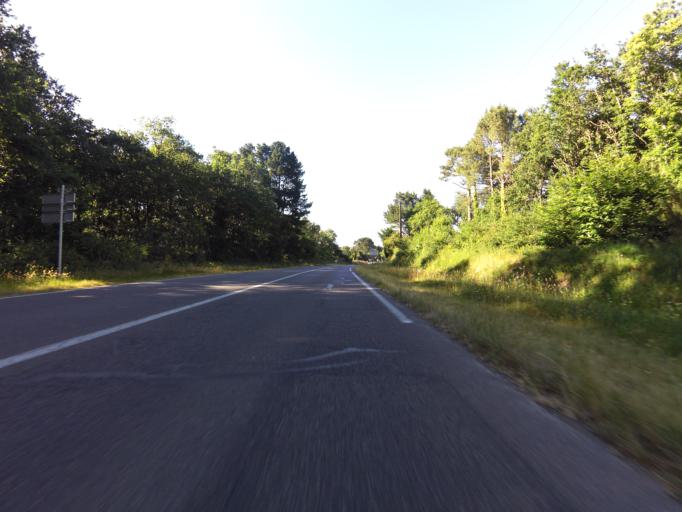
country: FR
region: Brittany
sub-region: Departement du Morbihan
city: Ferel
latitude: 47.4913
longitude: -2.3883
